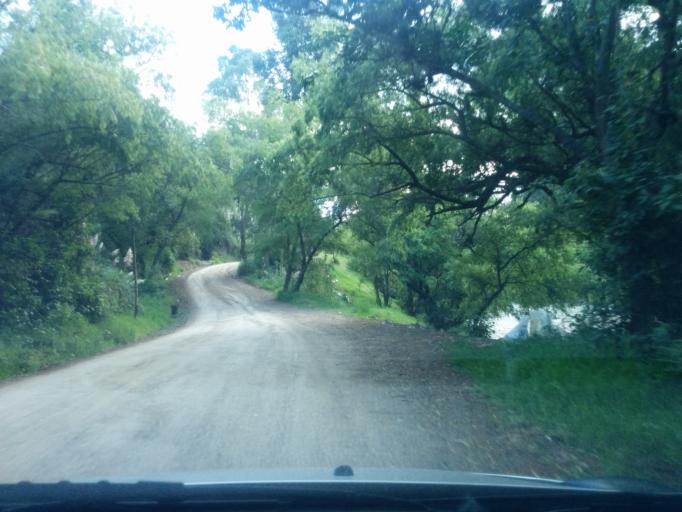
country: EC
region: Azuay
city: Cuenca
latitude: -2.8902
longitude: -78.9569
